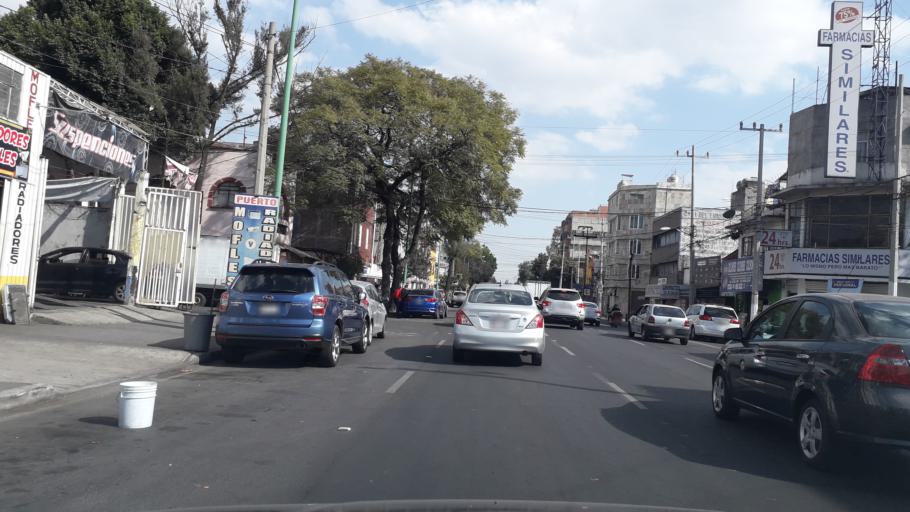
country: MX
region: Mexico City
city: Gustavo A. Madero
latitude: 19.4778
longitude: -99.1184
